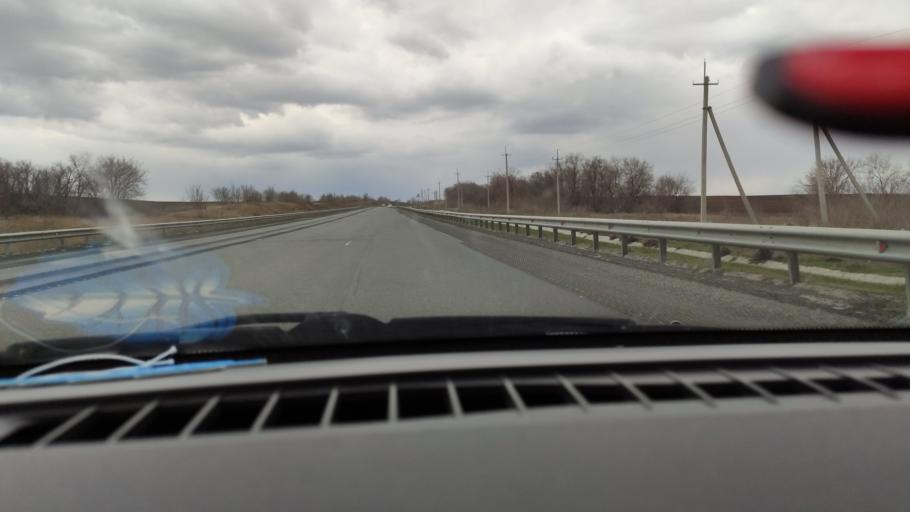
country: RU
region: Saratov
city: Shumeyka
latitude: 51.7784
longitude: 46.1199
